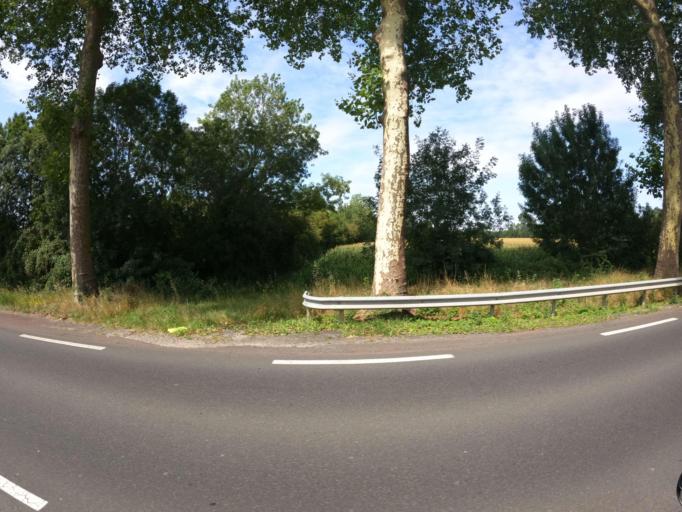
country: FR
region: Poitou-Charentes
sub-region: Departement des Deux-Sevres
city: Frontenay-Rohan-Rohan
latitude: 46.2716
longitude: -0.5272
